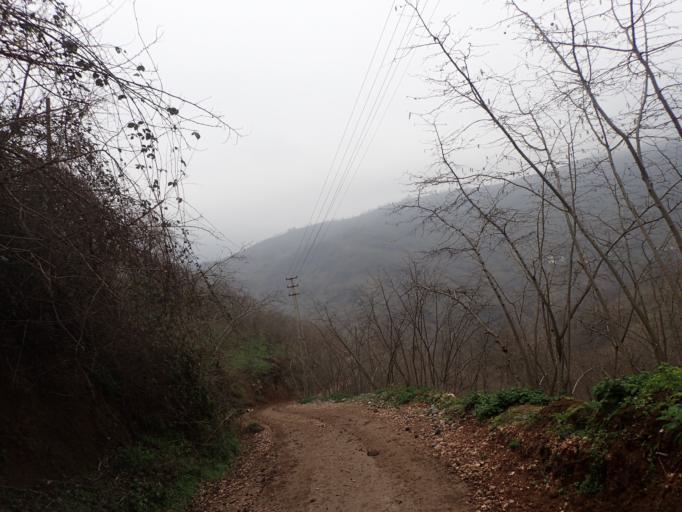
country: TR
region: Ordu
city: Camas
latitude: 40.9219
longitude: 37.5633
